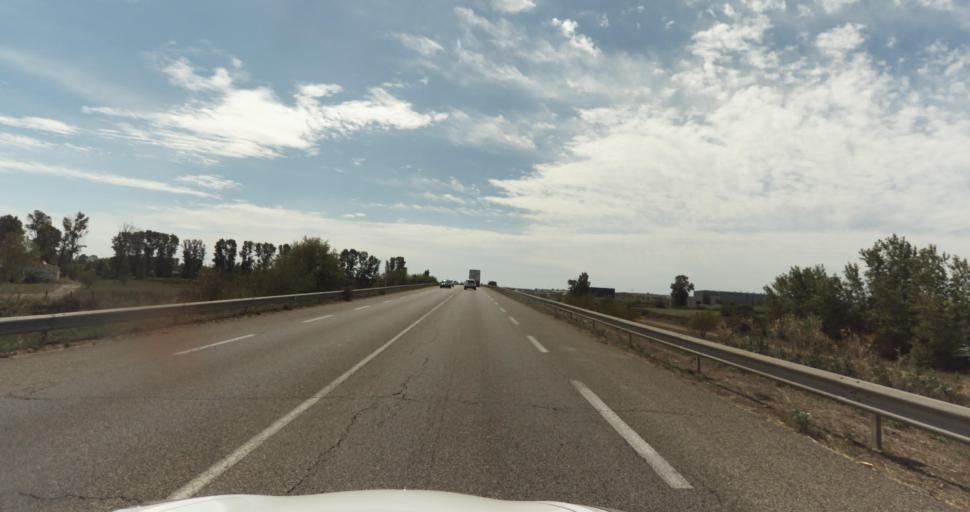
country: FR
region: Provence-Alpes-Cote d'Azur
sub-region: Departement des Bouches-du-Rhone
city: Istres
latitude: 43.5373
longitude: 4.9576
